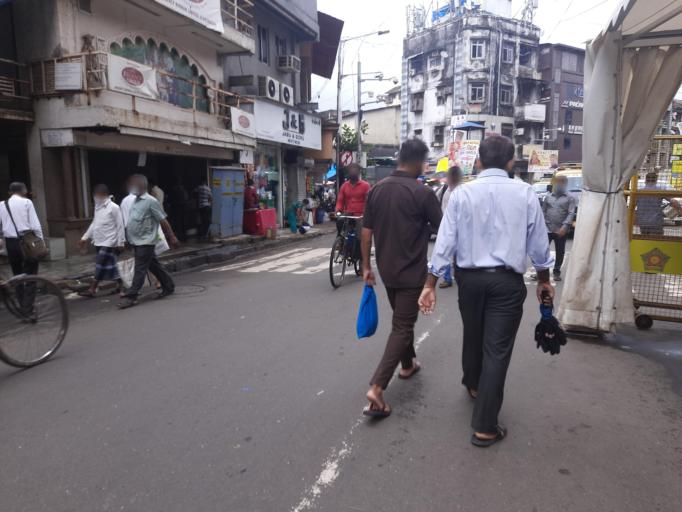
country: IN
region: Maharashtra
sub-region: Mumbai Suburban
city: Mumbai
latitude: 18.9522
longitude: 72.8297
